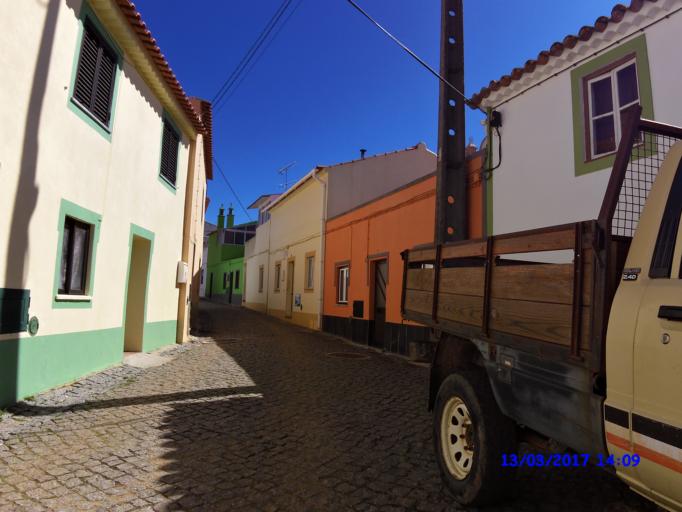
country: PT
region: Faro
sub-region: Monchique
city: Monchique
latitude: 37.3109
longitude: -8.6685
